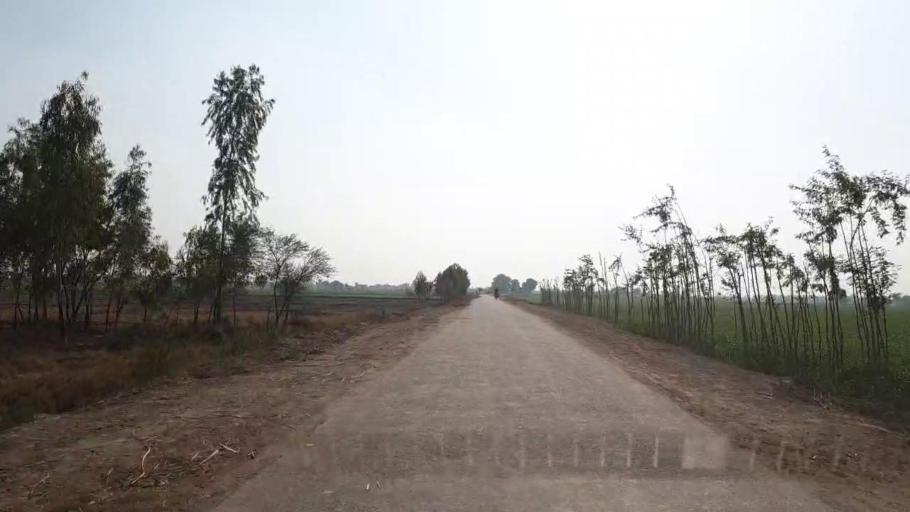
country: PK
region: Sindh
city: Tando Adam
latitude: 25.6680
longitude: 68.5790
